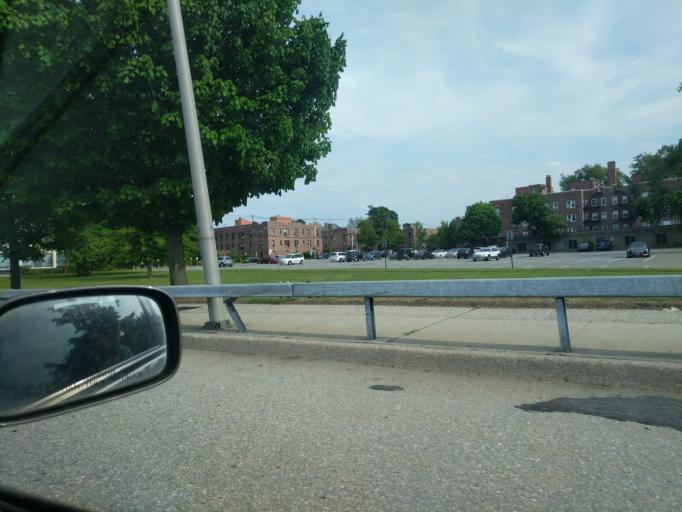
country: US
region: New York
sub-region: Nassau County
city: Rockville Centre
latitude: 40.6565
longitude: -73.6521
